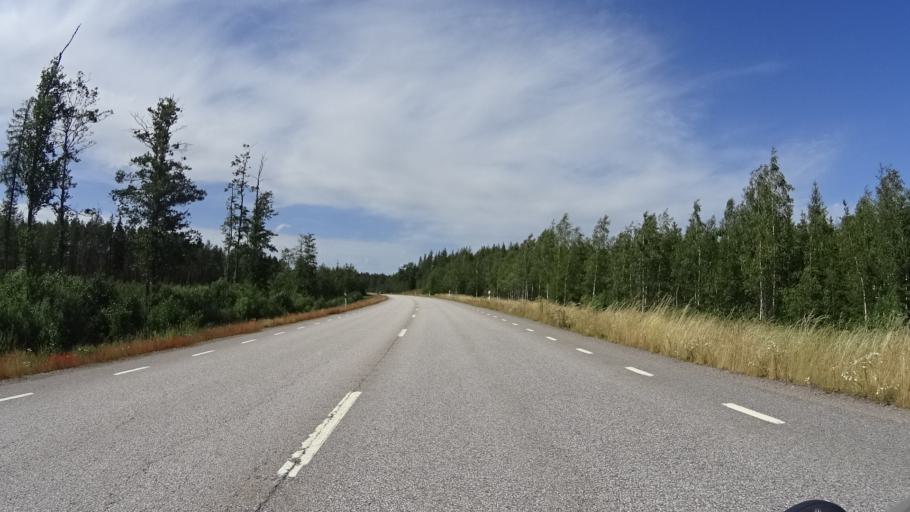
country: SE
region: Kalmar
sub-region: Vasterviks Kommun
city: Gamleby
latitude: 57.9538
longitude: 16.3769
